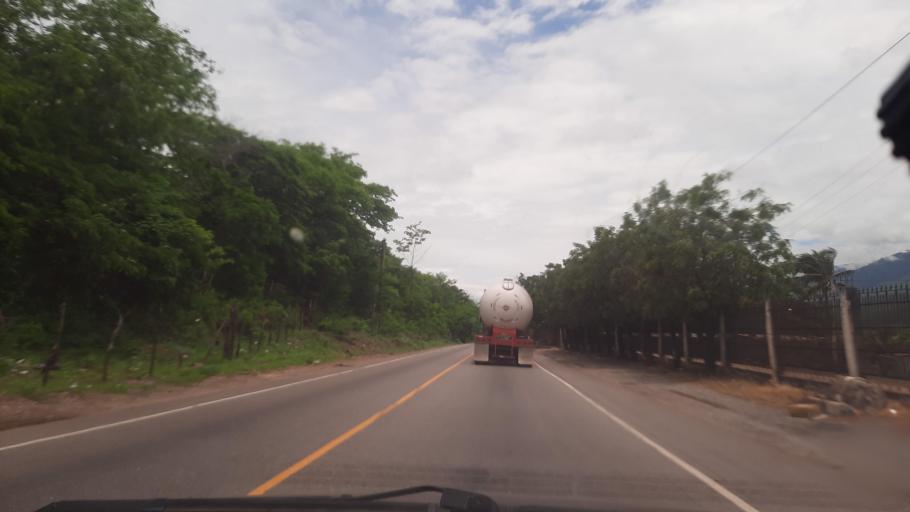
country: GT
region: Zacapa
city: Rio Hondo
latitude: 15.0755
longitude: -89.4976
